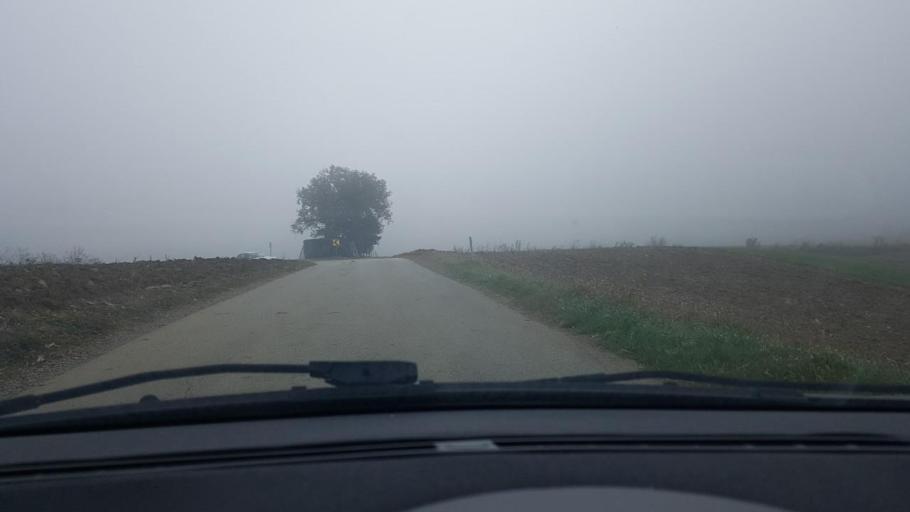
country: HR
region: Varazdinska
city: Lepoglava
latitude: 46.1521
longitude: 16.0311
